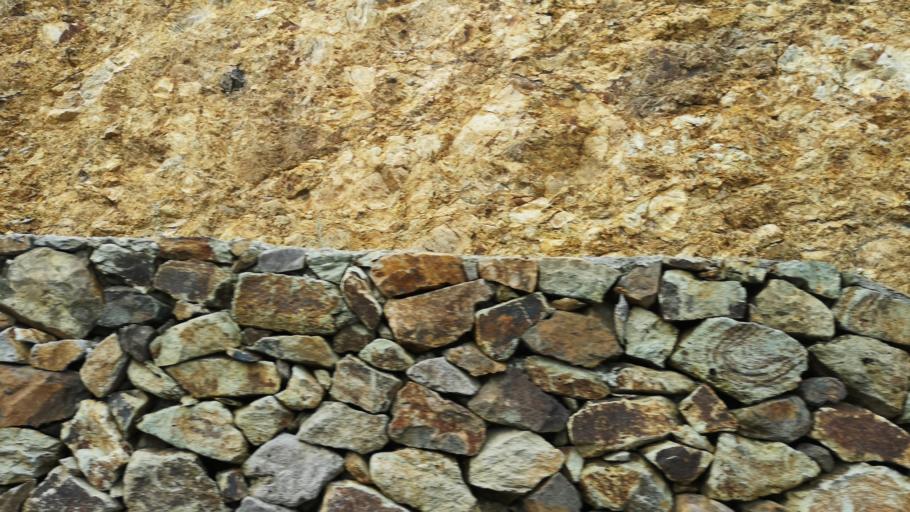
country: ES
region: Canary Islands
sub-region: Provincia de Santa Cruz de Tenerife
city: Vallehermosa
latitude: 28.1775
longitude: -17.2687
